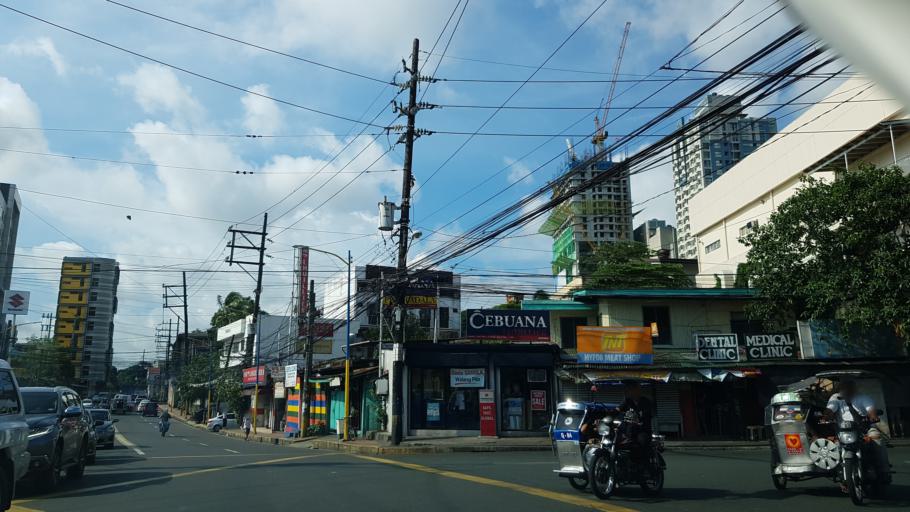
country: PH
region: Metro Manila
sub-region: Mandaluyong
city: Mandaluyong City
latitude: 14.5876
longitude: 121.0379
